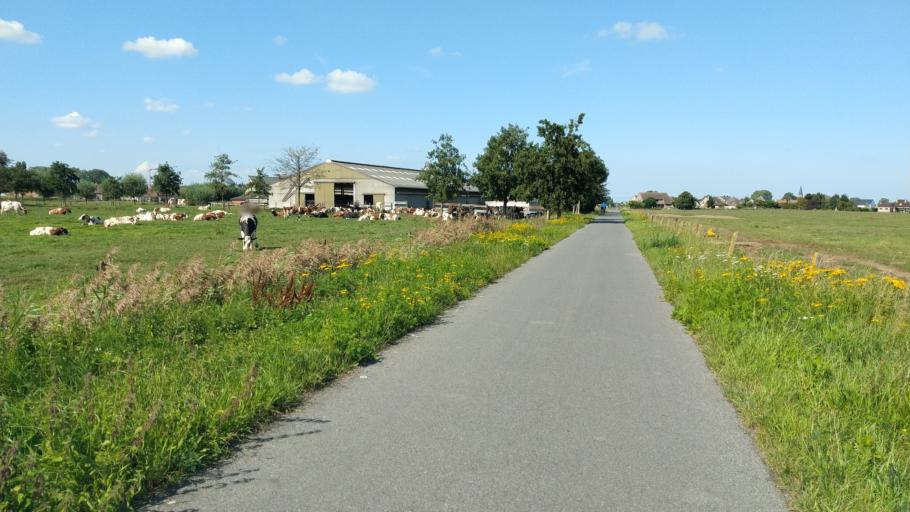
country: BE
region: Flanders
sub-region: Provincie Oost-Vlaanderen
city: Assenede
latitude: 51.2177
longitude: 3.7698
